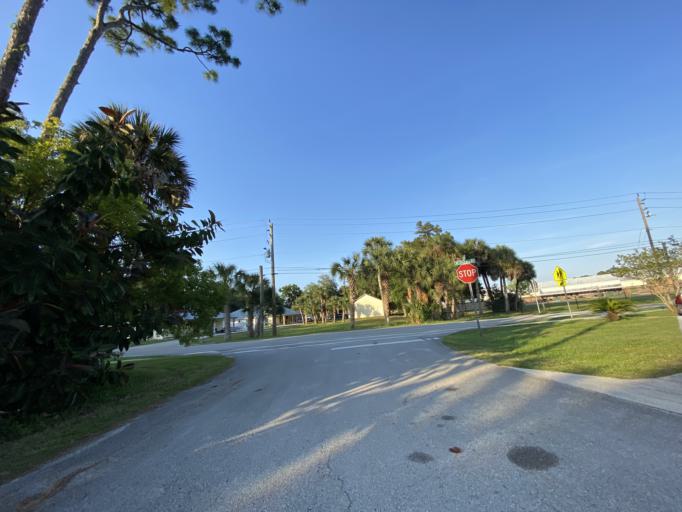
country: US
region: Florida
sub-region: Volusia County
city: Port Orange
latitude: 29.1473
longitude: -81.0030
